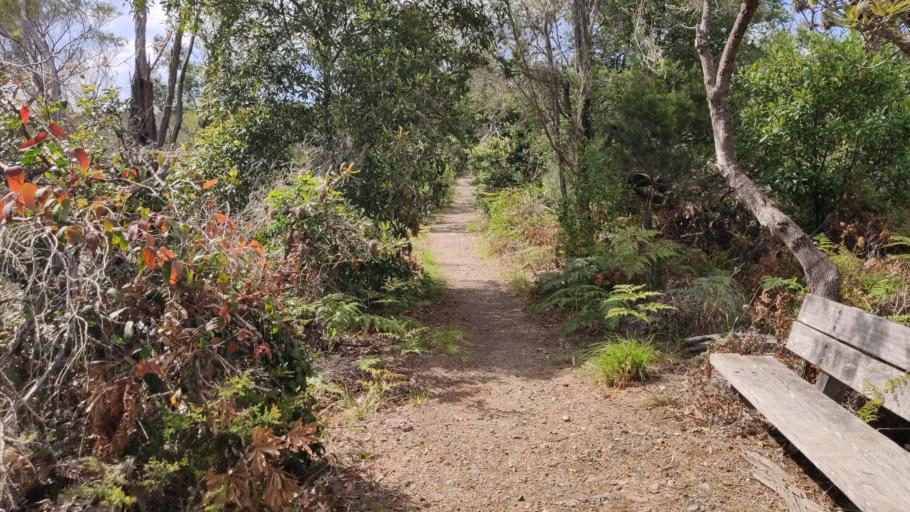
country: AU
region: New South Wales
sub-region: Port Macquarie-Hastings
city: North Haven
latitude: -31.6444
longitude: 152.8369
